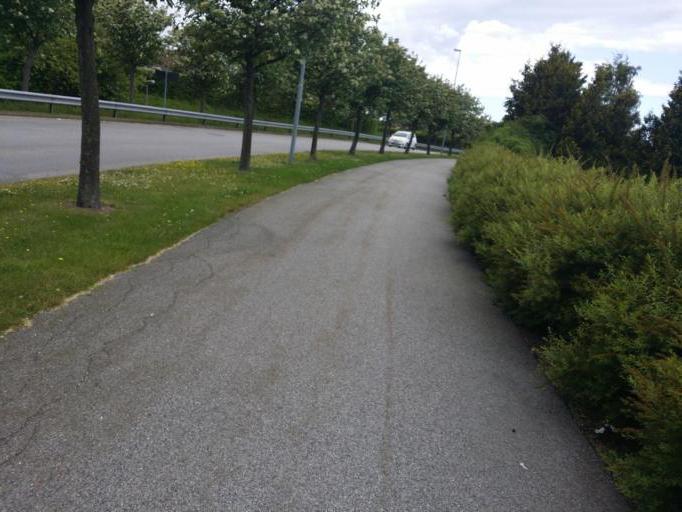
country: SE
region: Skane
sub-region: Burlovs Kommun
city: Arloev
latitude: 55.5993
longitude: 13.0933
